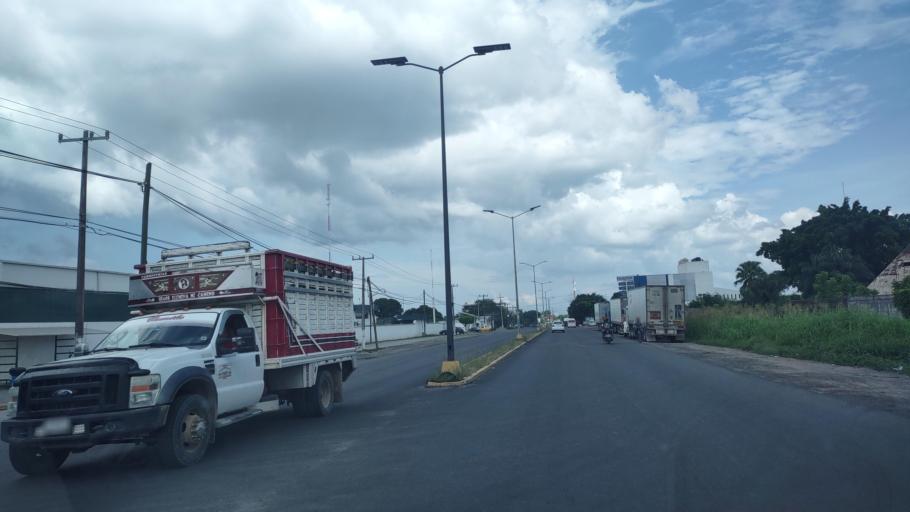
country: MX
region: Veracruz
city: Martinez de la Torre
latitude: 20.0698
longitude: -97.0709
